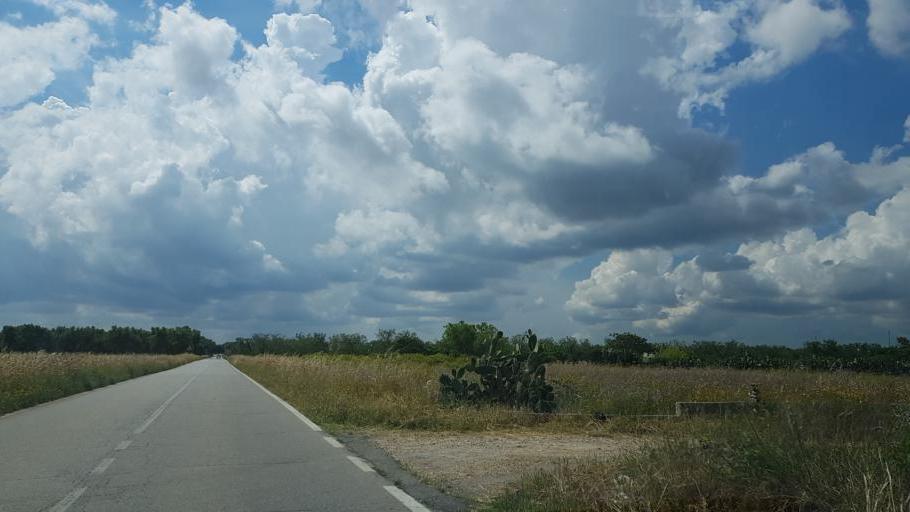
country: IT
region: Apulia
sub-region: Provincia di Brindisi
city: Mesagne
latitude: 40.5216
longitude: 17.8218
